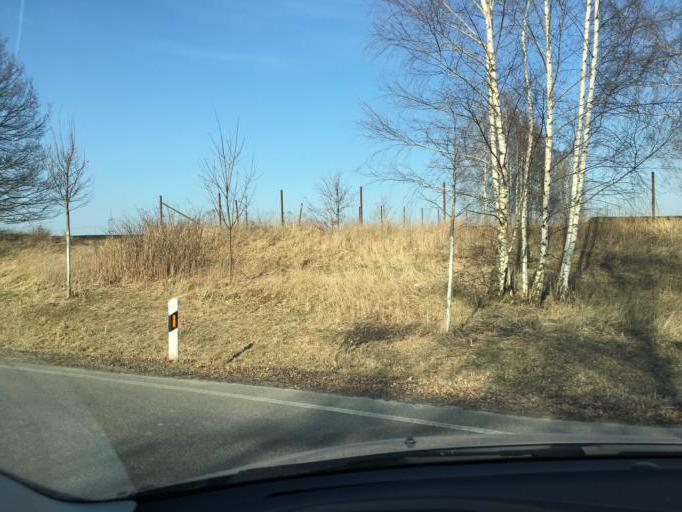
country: DE
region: Saxony
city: Waldenburg
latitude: 50.8813
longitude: 12.5896
